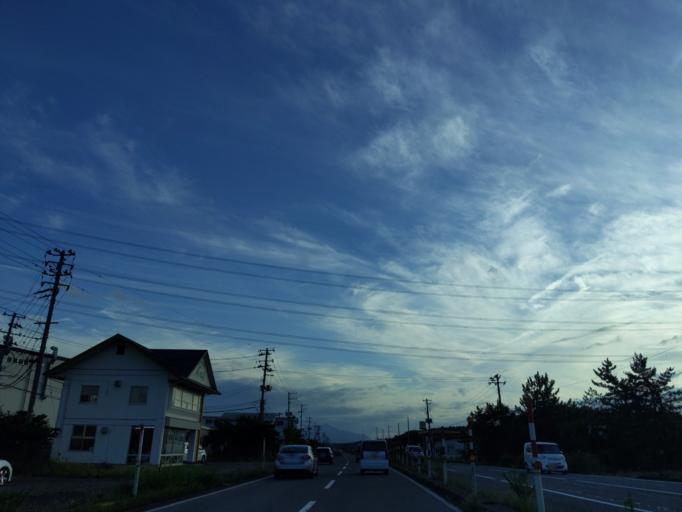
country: JP
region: Niigata
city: Kashiwazaki
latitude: 37.4437
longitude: 138.6337
